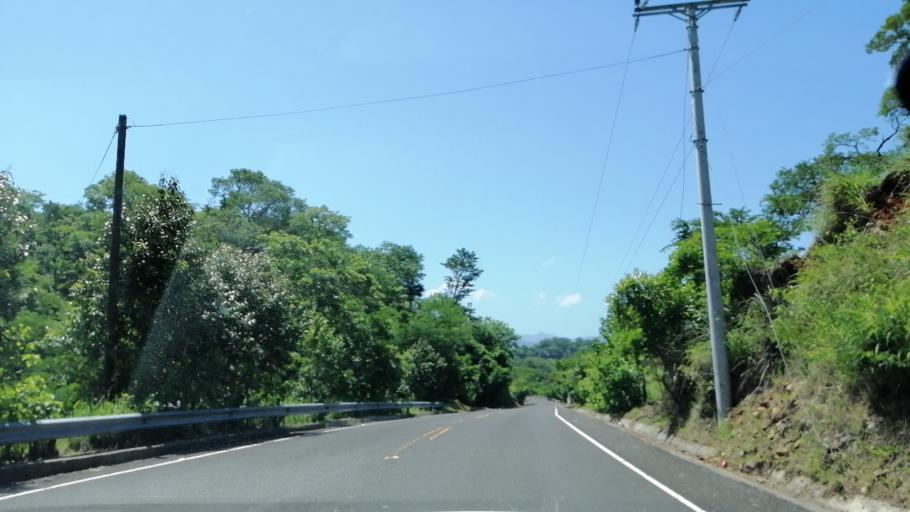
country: SV
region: San Miguel
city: Sesori
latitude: 13.8064
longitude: -88.3874
